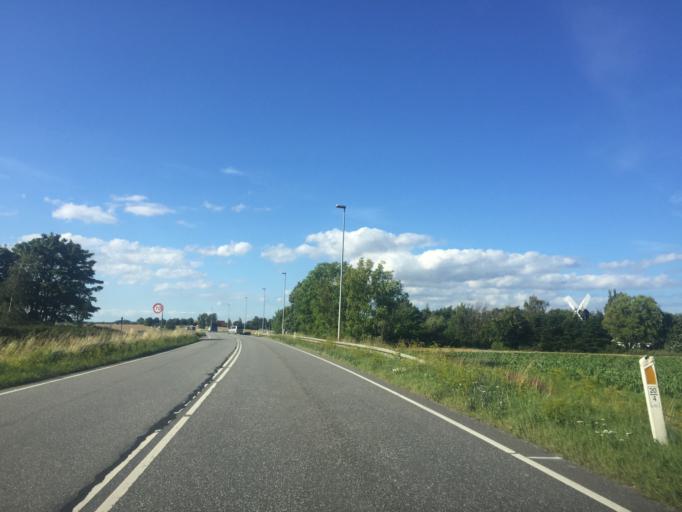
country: DK
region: Zealand
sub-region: Guldborgsund Kommune
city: Nykobing Falster
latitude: 54.6003
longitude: 11.9354
